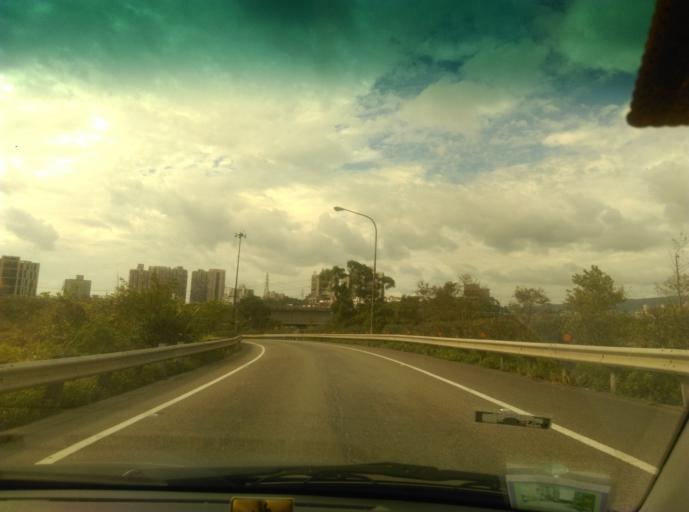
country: TW
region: Taiwan
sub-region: Keelung
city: Keelung
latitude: 25.0745
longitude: 121.6482
